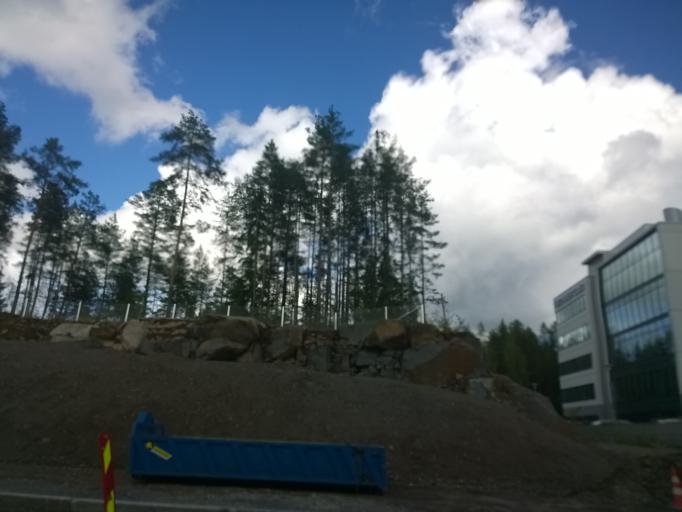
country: FI
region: Pirkanmaa
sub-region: Tampere
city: Tampere
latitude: 61.4478
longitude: 23.8547
